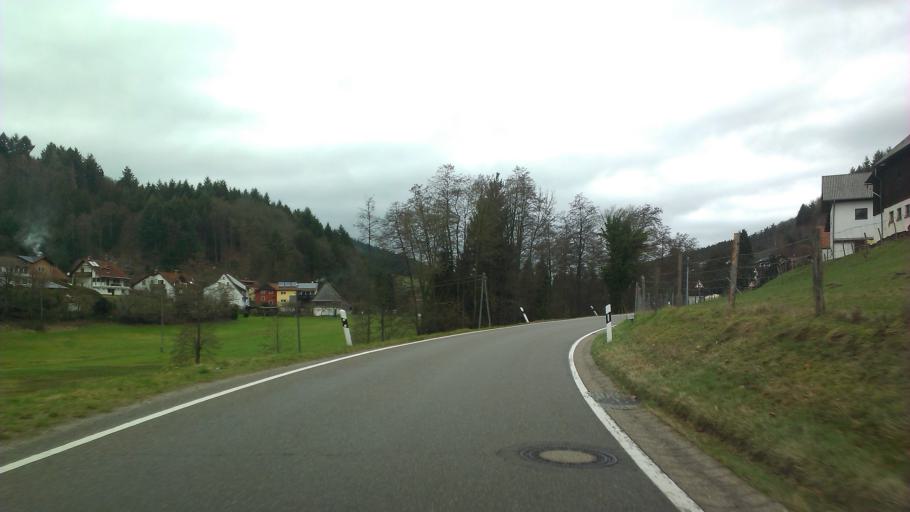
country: DE
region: Baden-Wuerttemberg
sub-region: Karlsruhe Region
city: Heiligkreuzsteinach
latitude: 49.4991
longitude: 8.8110
